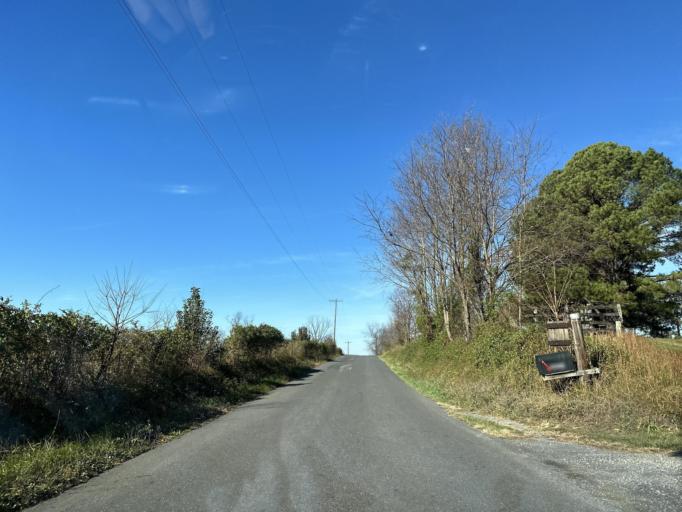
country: US
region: Virginia
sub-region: Augusta County
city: Weyers Cave
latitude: 38.2169
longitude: -78.9150
